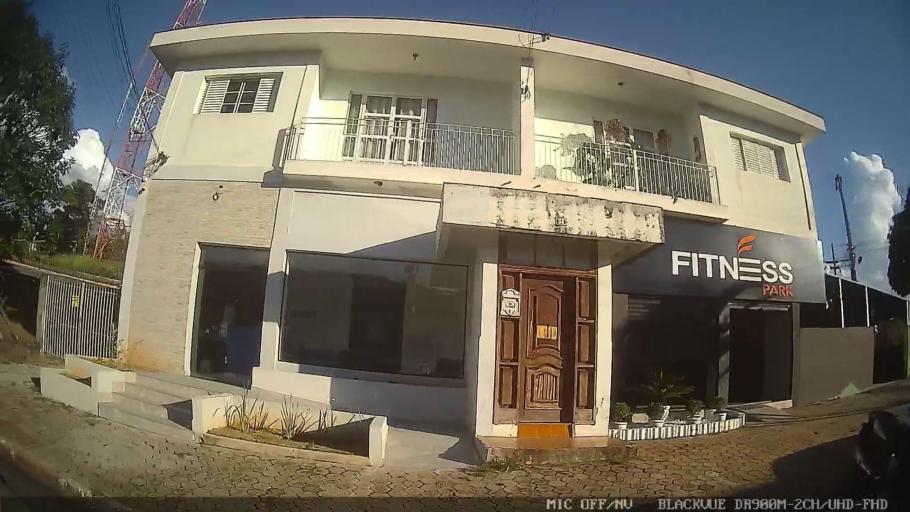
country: BR
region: Minas Gerais
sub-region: Extrema
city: Extrema
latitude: -22.8906
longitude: -46.4159
